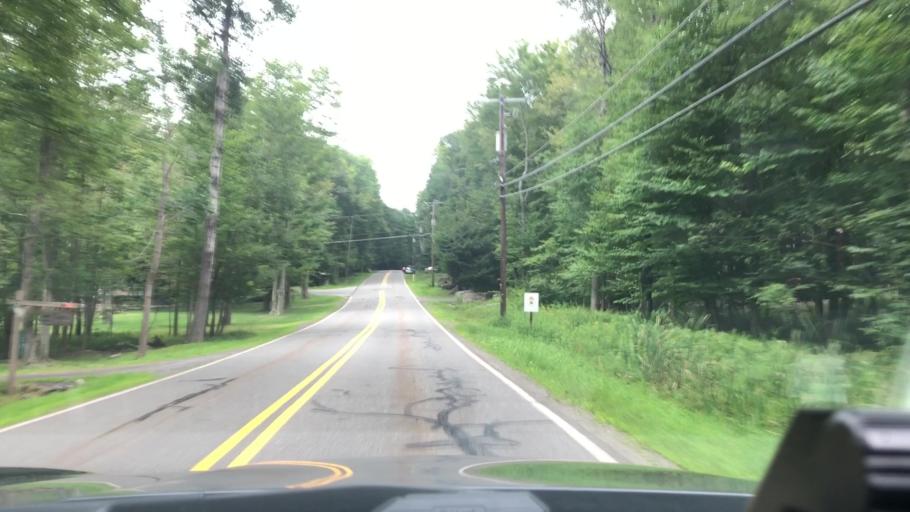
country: US
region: Pennsylvania
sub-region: Lackawanna County
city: Moscow
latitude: 41.2507
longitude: -75.4905
